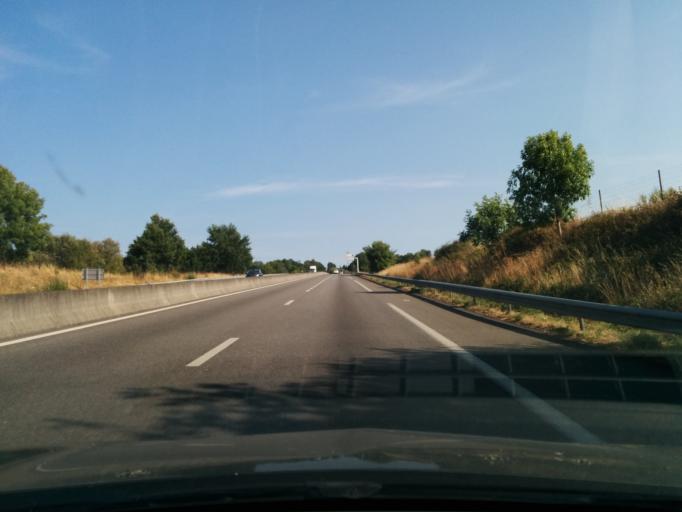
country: FR
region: Limousin
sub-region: Departement de la Haute-Vienne
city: Pierre-Buffiere
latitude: 45.7170
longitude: 1.3540
